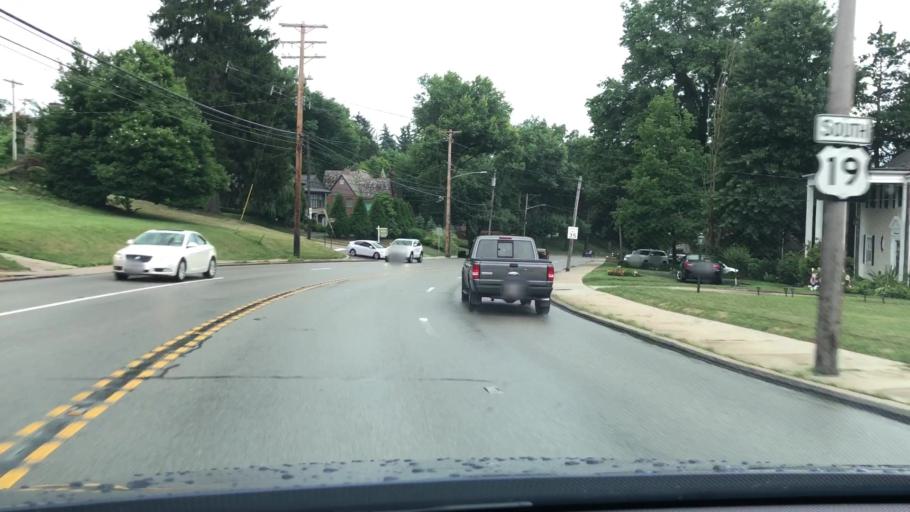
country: US
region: Pennsylvania
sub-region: Allegheny County
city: Mount Lebanon
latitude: 40.3629
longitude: -80.0467
